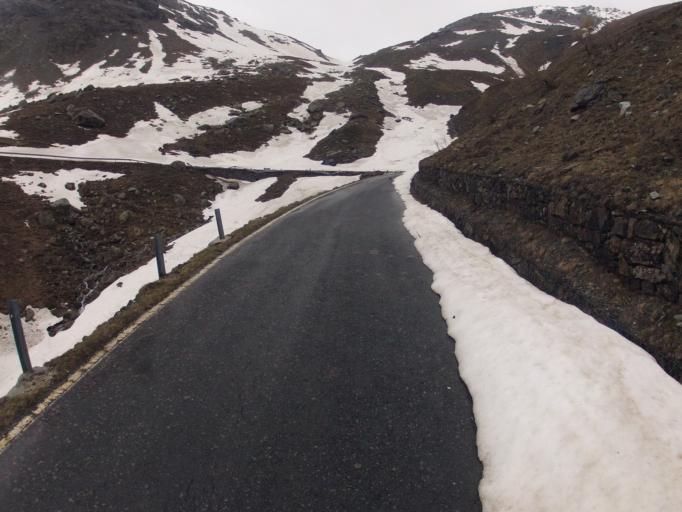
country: IT
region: Piedmont
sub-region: Provincia di Cuneo
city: Crissolo
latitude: 44.7038
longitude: 7.1107
